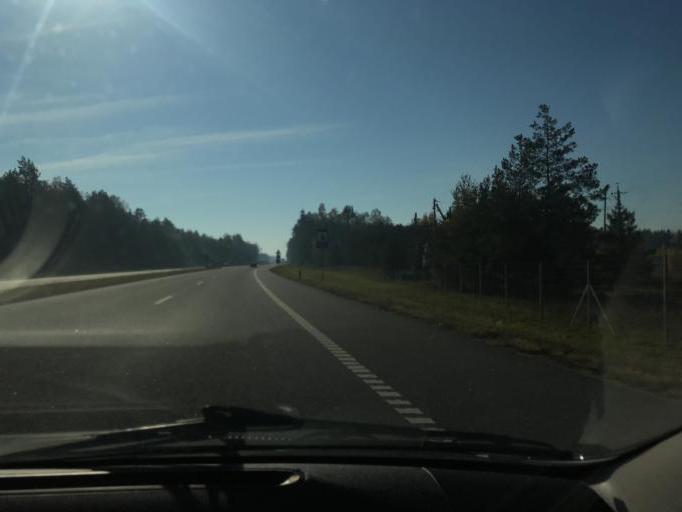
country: BY
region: Minsk
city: Slutsk
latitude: 53.2864
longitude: 27.5495
